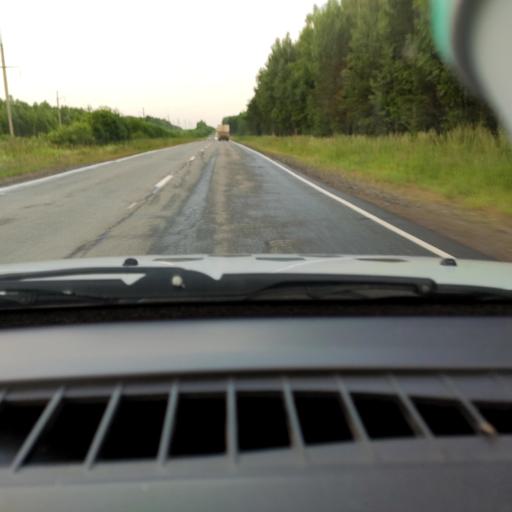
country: RU
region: Udmurtiya
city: Fakel
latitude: 57.6837
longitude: 53.0139
